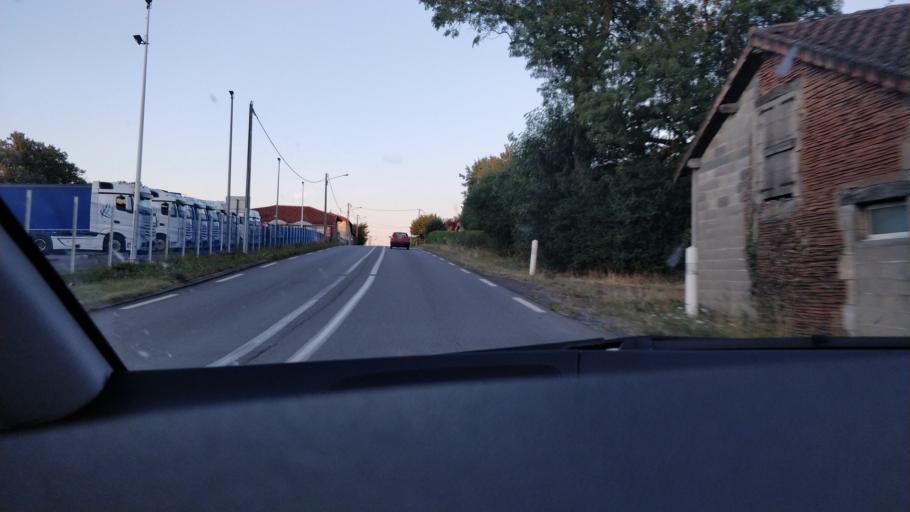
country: FR
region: Poitou-Charentes
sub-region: Departement de la Charente
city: Loubert
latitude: 45.8648
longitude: 0.5396
